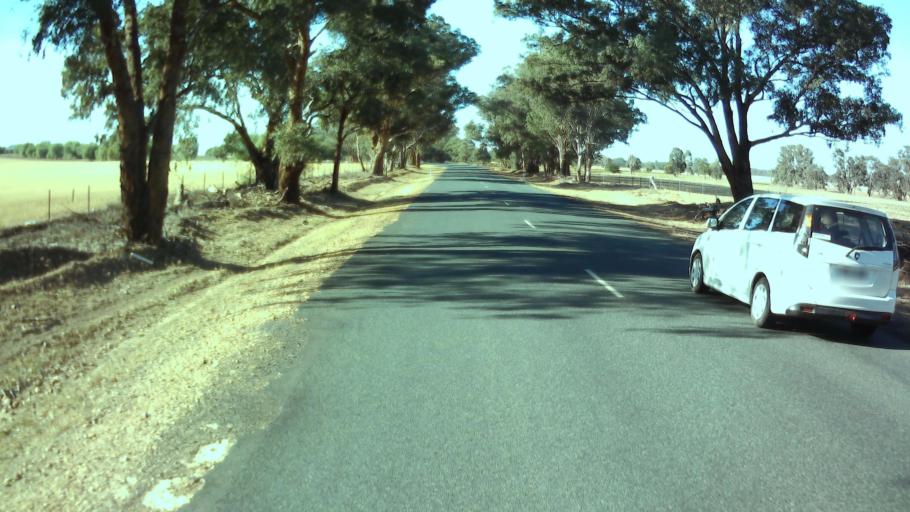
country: AU
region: New South Wales
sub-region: Weddin
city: Grenfell
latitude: -33.9780
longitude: 148.1409
